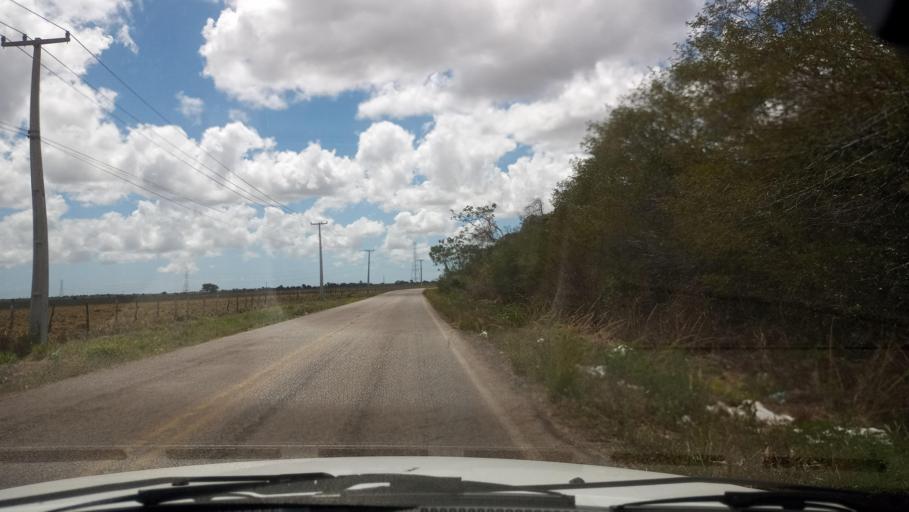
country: BR
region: Rio Grande do Norte
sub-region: Brejinho
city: Brejinho
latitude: -6.0409
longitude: -35.4186
